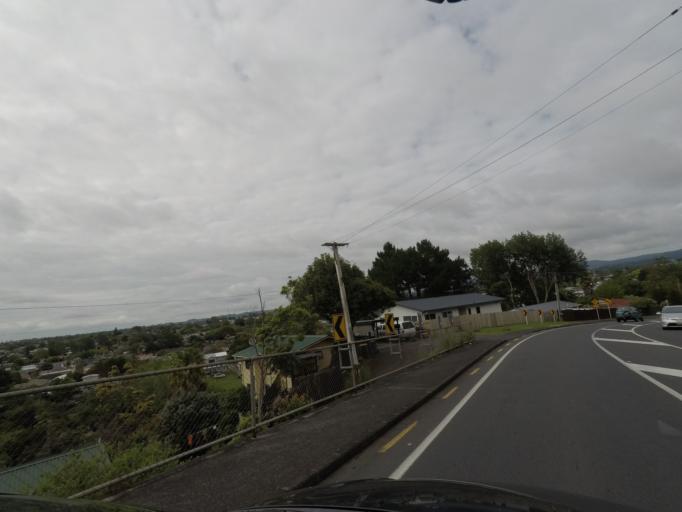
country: NZ
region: Auckland
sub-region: Auckland
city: Rosebank
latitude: -36.8564
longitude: 174.6110
